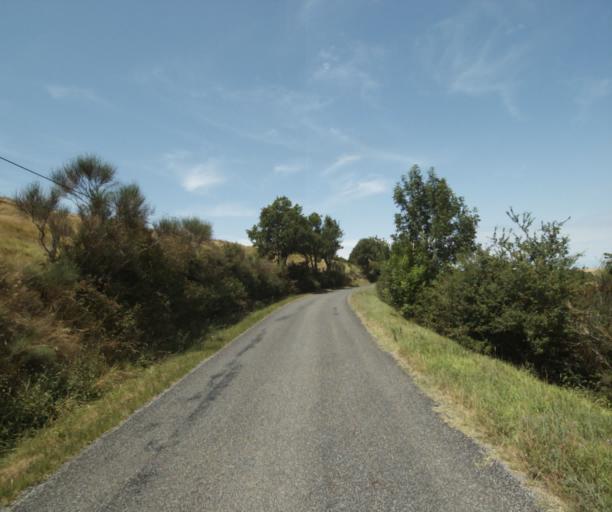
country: FR
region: Midi-Pyrenees
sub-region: Departement de la Haute-Garonne
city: Saint-Felix-Lauragais
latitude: 43.4395
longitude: 1.8960
